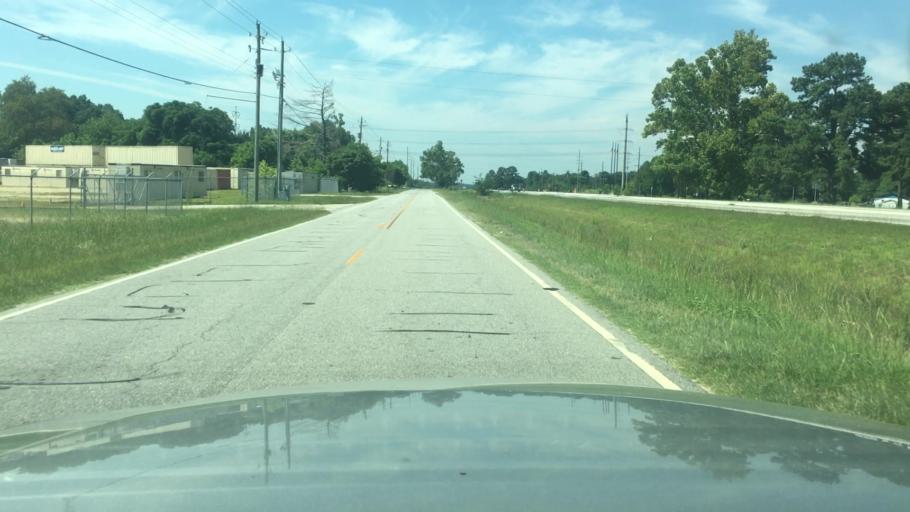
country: US
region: North Carolina
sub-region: Cumberland County
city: Hope Mills
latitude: 34.9795
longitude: -78.9077
